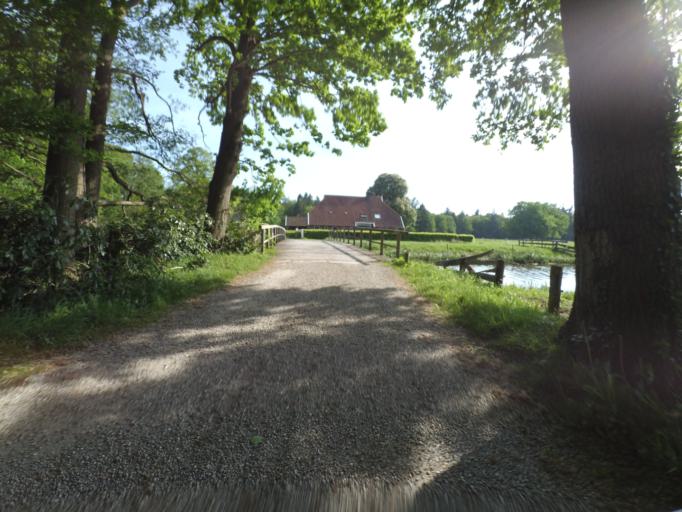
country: NL
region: Overijssel
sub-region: Gemeente Oldenzaal
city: Oldenzaal
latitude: 52.3723
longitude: 6.9857
